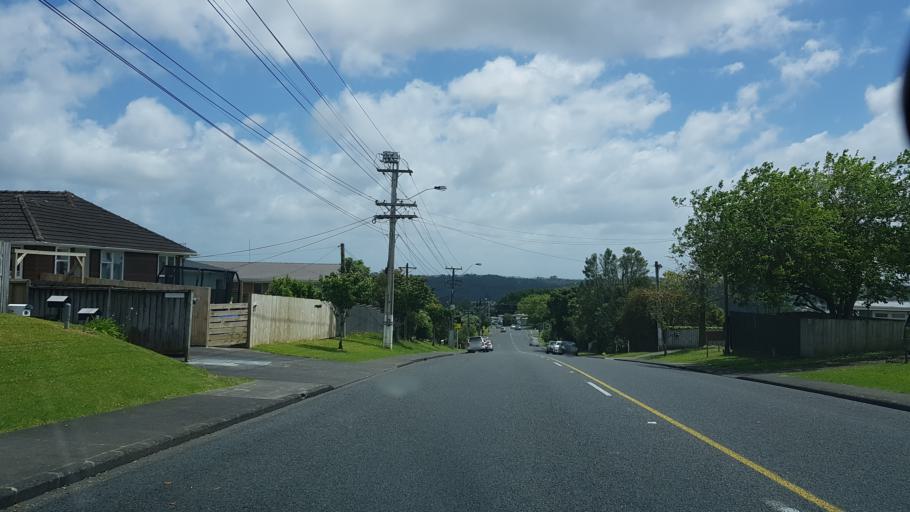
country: NZ
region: Auckland
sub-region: Auckland
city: North Shore
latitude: -36.8032
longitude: 174.7038
